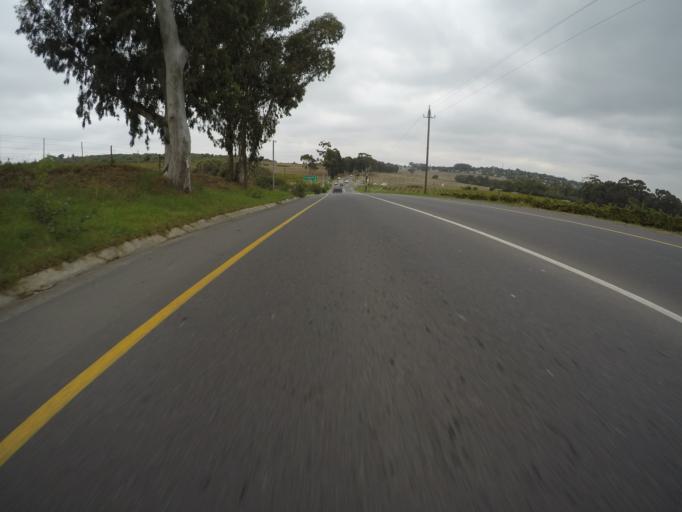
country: ZA
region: Western Cape
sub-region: City of Cape Town
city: Kraaifontein
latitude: -33.8427
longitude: 18.6217
